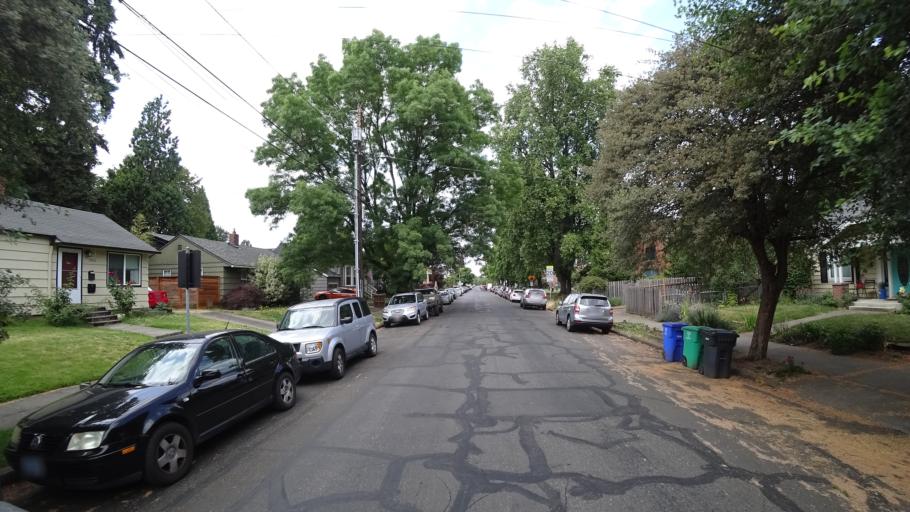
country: US
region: Oregon
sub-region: Multnomah County
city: Portland
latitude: 45.4942
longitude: -122.6514
